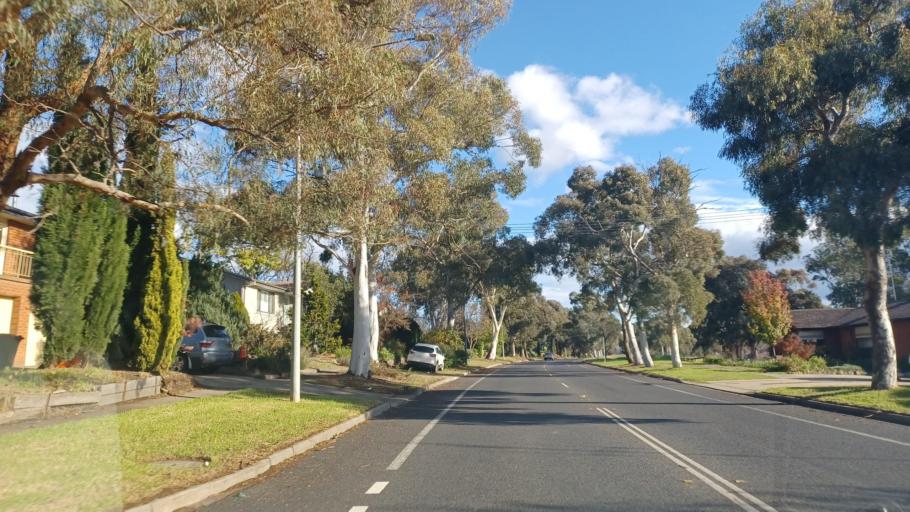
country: AU
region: Australian Capital Territory
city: Belconnen
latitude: -35.1903
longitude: 149.0462
